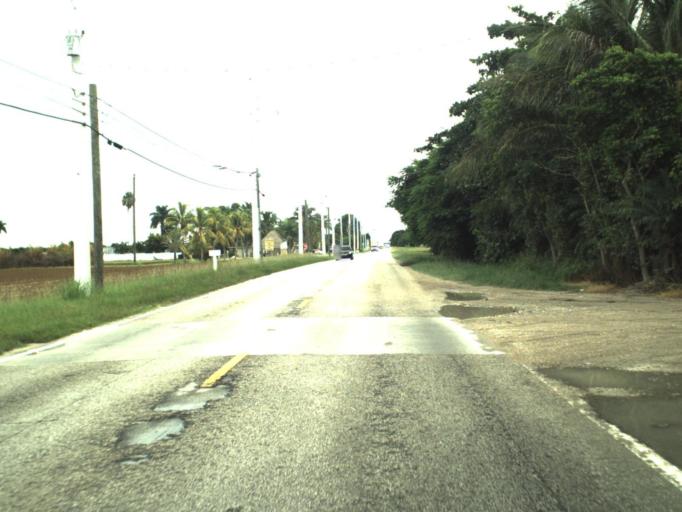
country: US
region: Florida
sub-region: Miami-Dade County
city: Florida City
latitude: 25.4248
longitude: -80.5014
